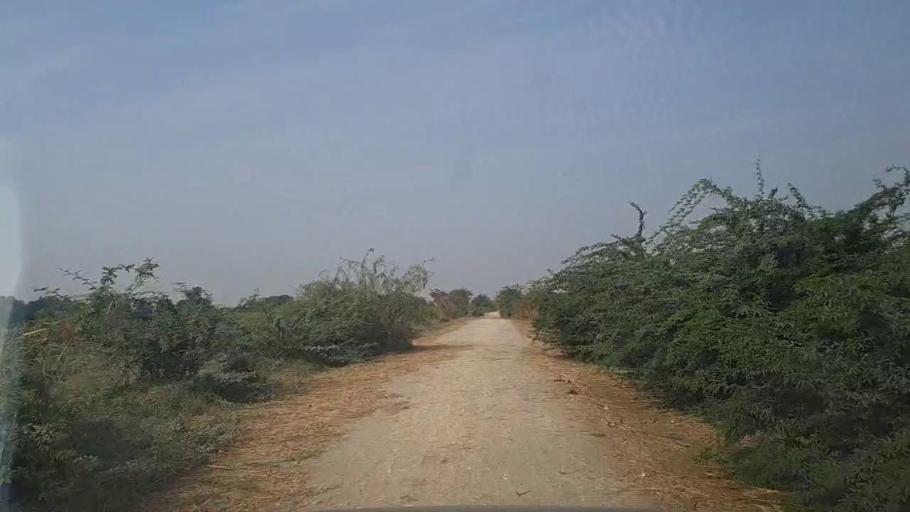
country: PK
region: Sindh
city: Bulri
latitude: 24.9789
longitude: 68.2974
